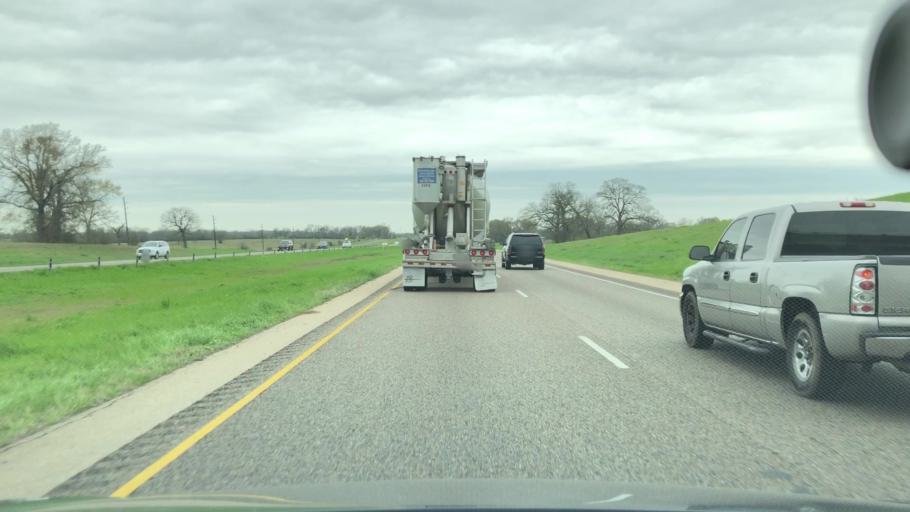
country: US
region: Texas
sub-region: Madison County
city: Madisonville
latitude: 31.0483
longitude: -95.9461
